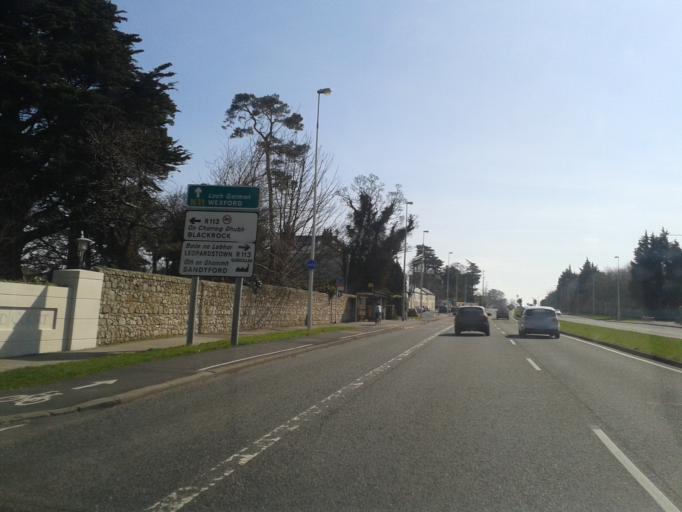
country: IE
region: Leinster
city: Foxrock
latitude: 53.2810
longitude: -6.1910
